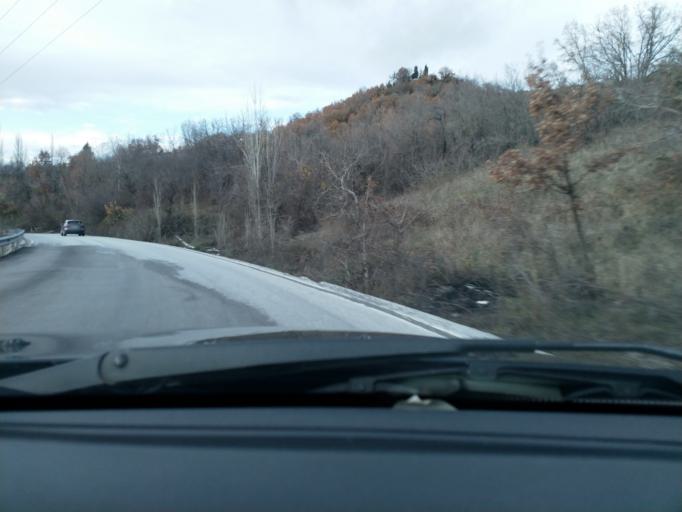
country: GR
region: Epirus
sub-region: Nomos Ioanninon
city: Metsovo
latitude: 39.7902
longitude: 21.3765
